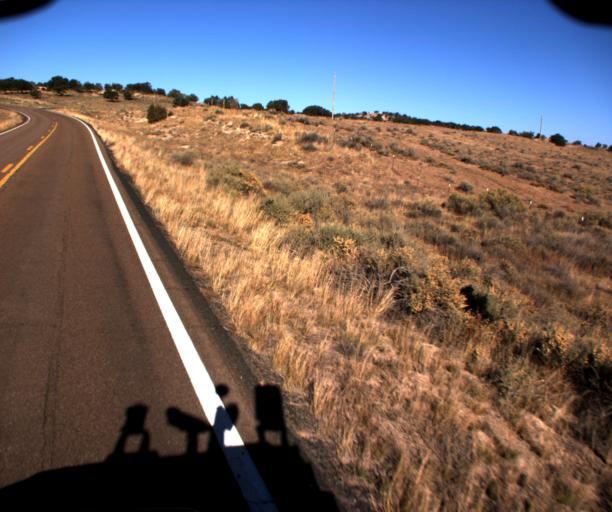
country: US
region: Arizona
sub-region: Navajo County
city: First Mesa
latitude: 35.7663
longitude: -109.9847
